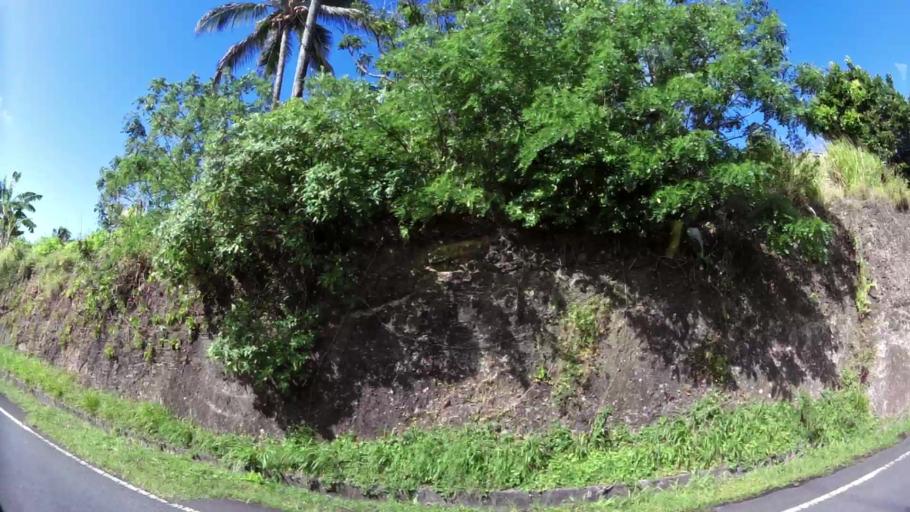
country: LC
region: Choiseul Quarter
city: Choiseul
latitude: 13.7979
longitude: -61.0380
